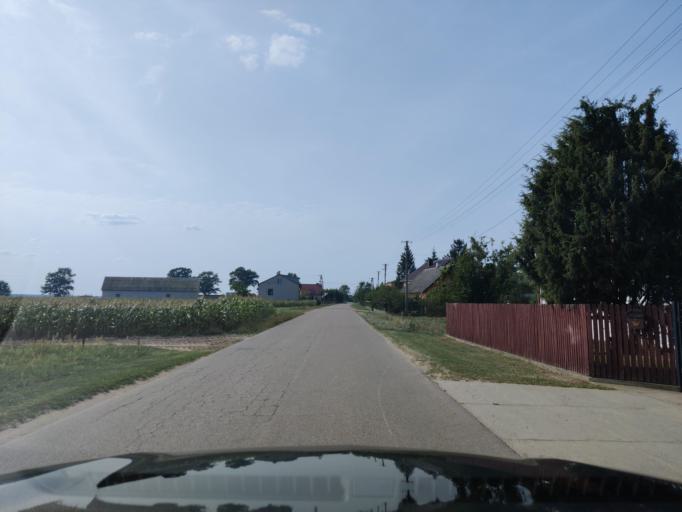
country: PL
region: Masovian Voivodeship
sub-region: Powiat pultuski
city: Obryte
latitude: 52.7636
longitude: 21.2928
